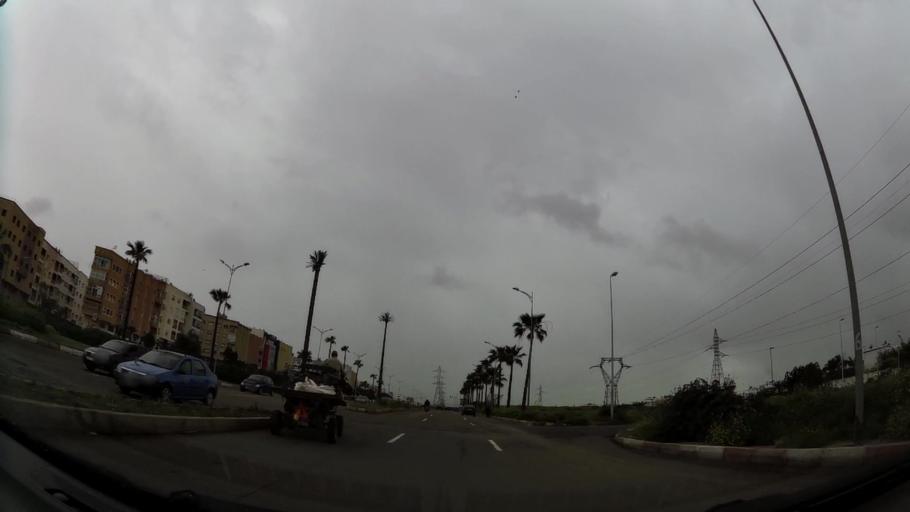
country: MA
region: Grand Casablanca
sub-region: Casablanca
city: Casablanca
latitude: 33.5340
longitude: -7.6175
